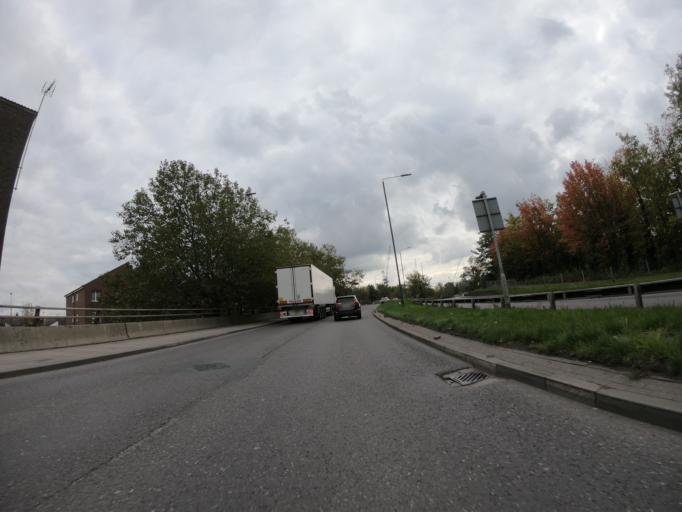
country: GB
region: England
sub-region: Greater London
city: Erith
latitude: 51.4769
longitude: 0.1812
